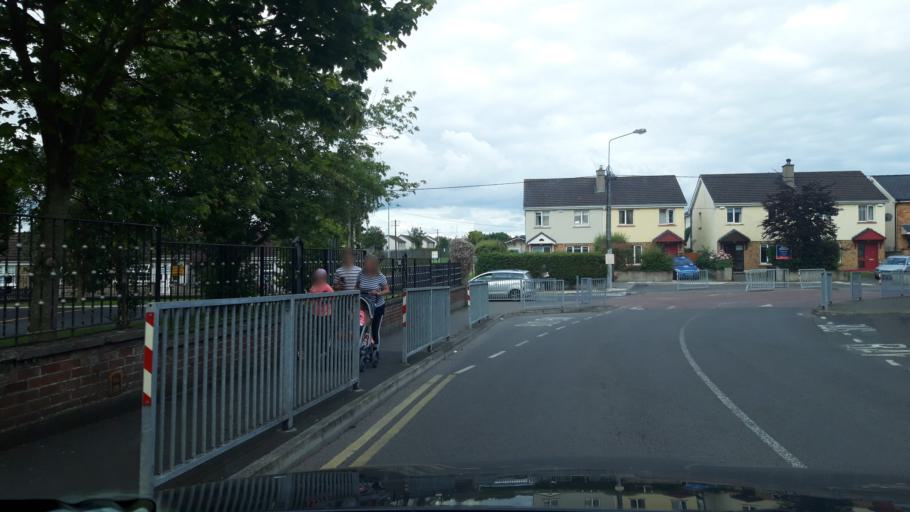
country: IE
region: Leinster
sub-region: Kildare
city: Athy
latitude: 52.9937
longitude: -6.9800
